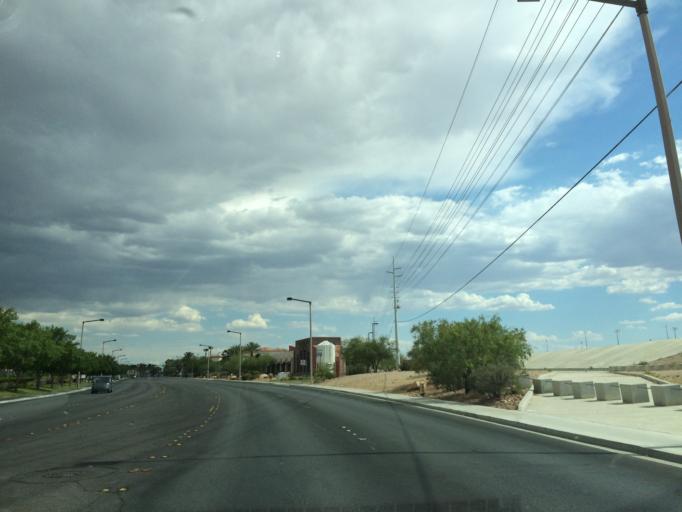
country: US
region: Nevada
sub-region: Clark County
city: Spring Valley
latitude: 36.2173
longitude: -115.2514
